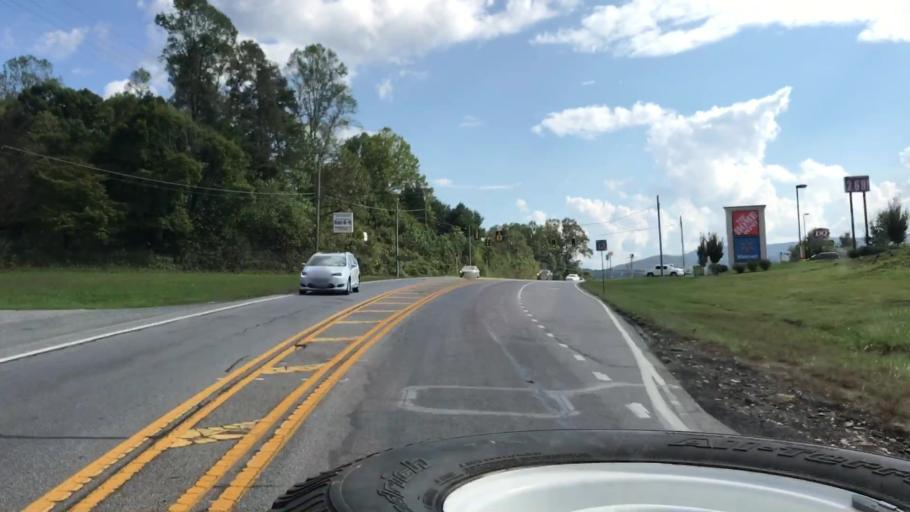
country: US
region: Georgia
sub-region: Fannin County
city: Blue Ridge
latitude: 34.8779
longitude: -84.3227
